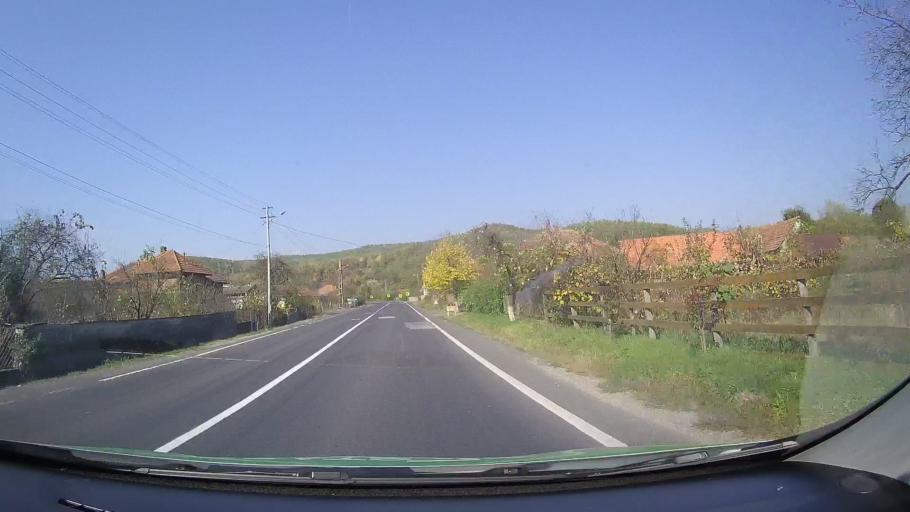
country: RO
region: Hunedoara
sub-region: Comuna Dobra
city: Dobra
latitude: 45.9488
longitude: 22.5892
